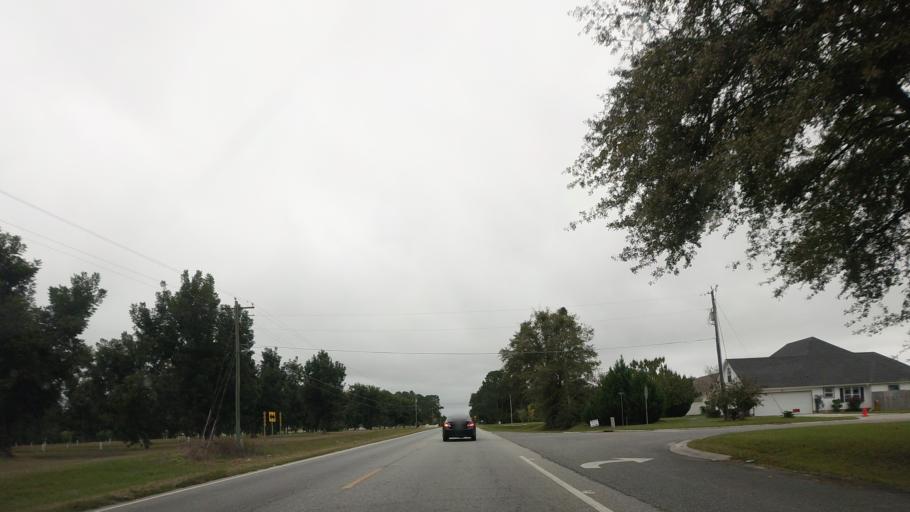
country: US
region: Georgia
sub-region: Berrien County
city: Ray City
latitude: 31.0348
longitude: -83.1978
